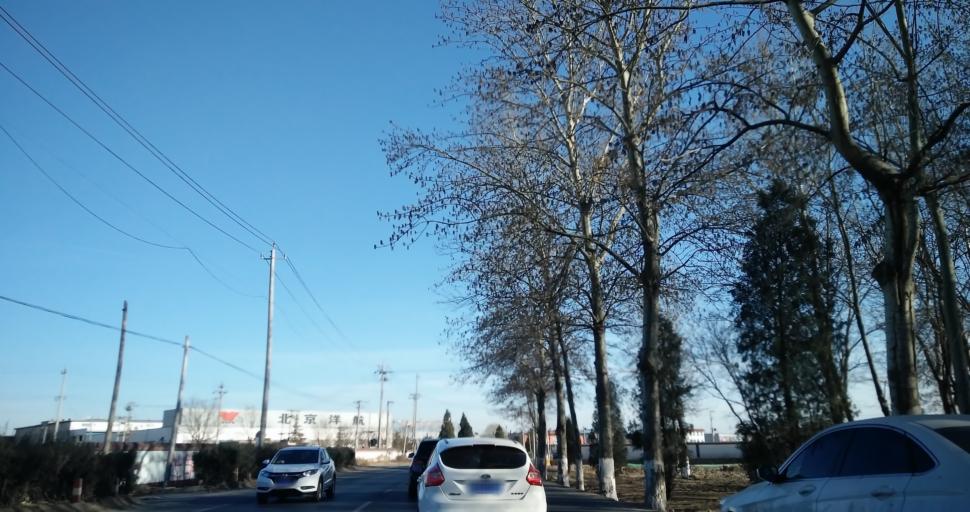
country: CN
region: Beijing
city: Yinghai
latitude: 39.7329
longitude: 116.4546
